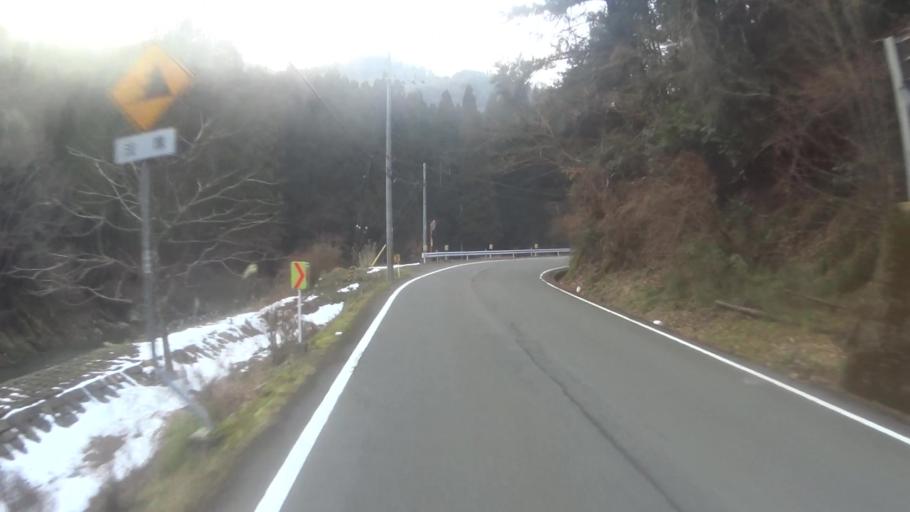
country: JP
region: Kyoto
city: Maizuru
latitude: 35.4091
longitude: 135.4617
